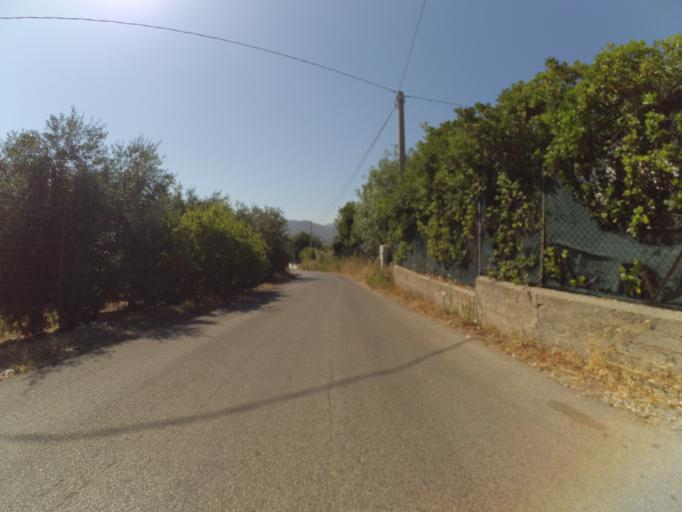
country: IT
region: Latium
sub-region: Provincia di Latina
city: Gaeta
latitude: 41.2261
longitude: 13.5424
